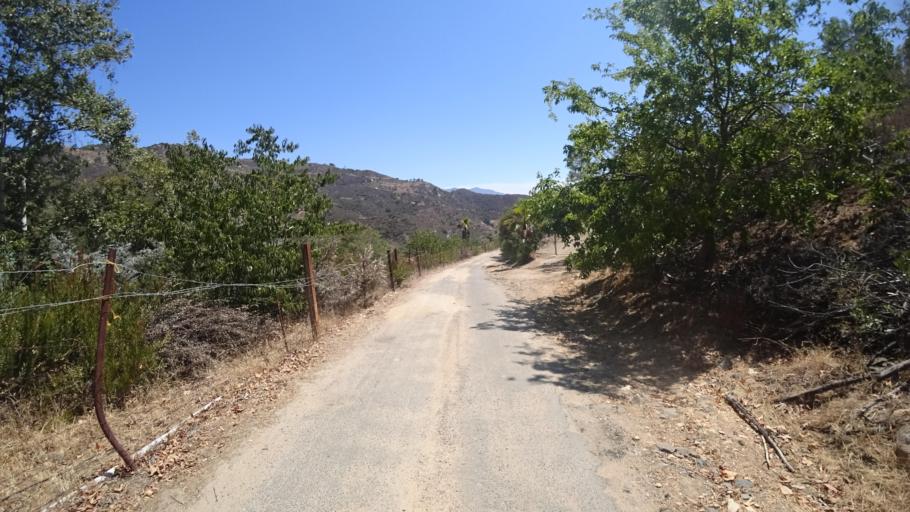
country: US
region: California
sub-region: San Diego County
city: Rainbow
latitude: 33.3835
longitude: -117.1115
